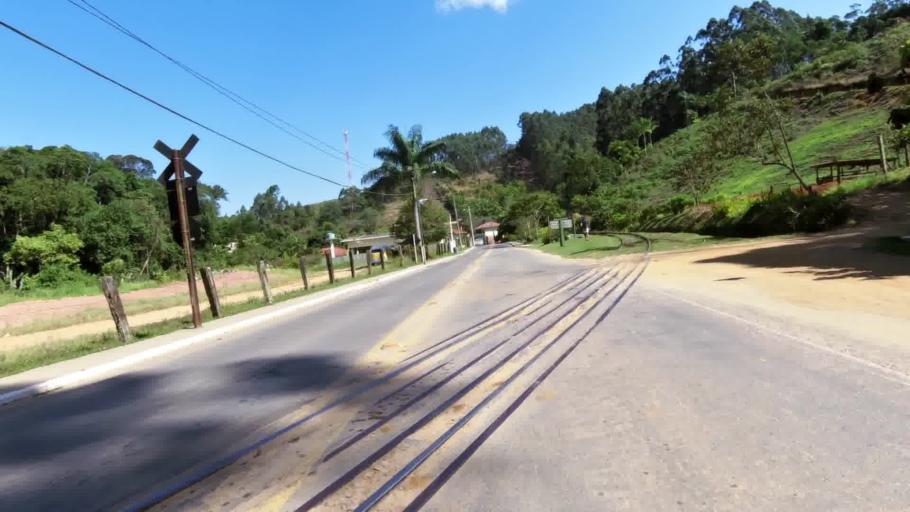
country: BR
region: Espirito Santo
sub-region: Marechal Floriano
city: Marechal Floriano
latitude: -20.4869
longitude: -40.7716
